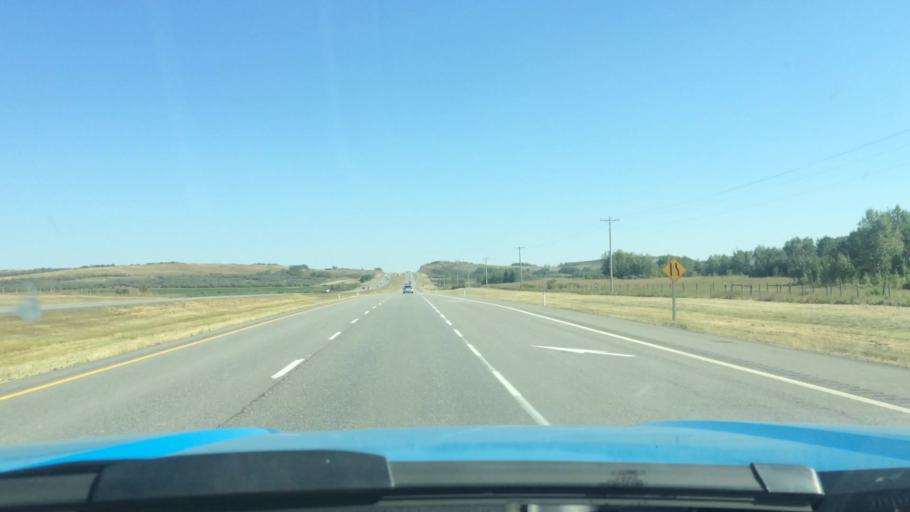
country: CA
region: Alberta
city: Cochrane
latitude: 51.1038
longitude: -114.6192
